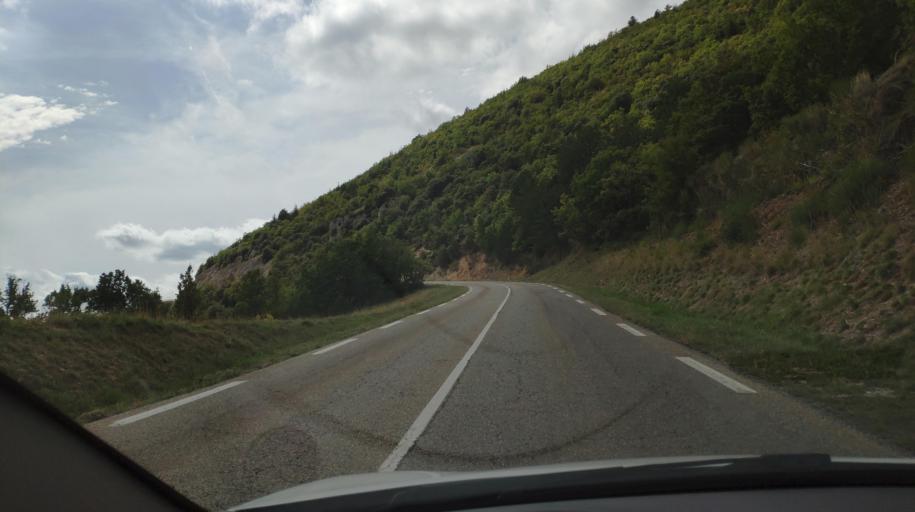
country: FR
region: Provence-Alpes-Cote d'Azur
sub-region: Departement du Vaucluse
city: Sault
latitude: 44.0888
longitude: 5.3683
